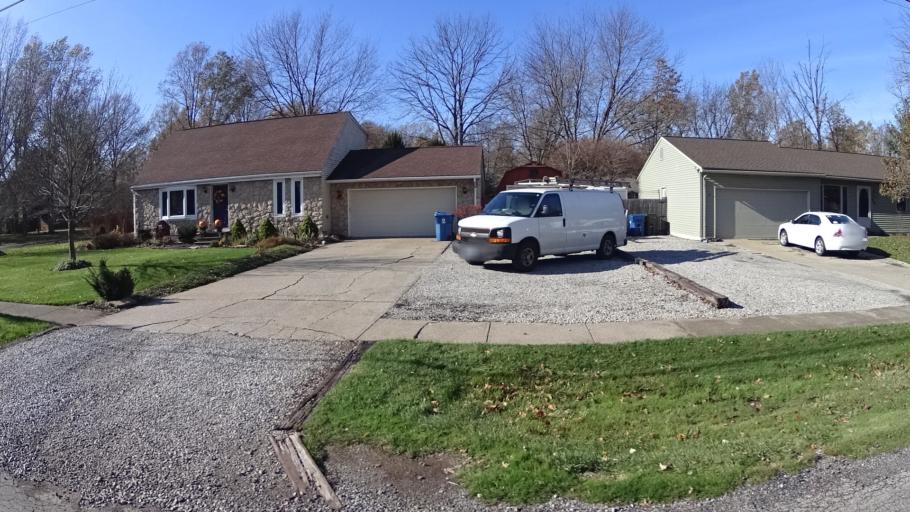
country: US
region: Ohio
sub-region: Lorain County
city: Sheffield Lake
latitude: 41.4930
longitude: -82.0809
